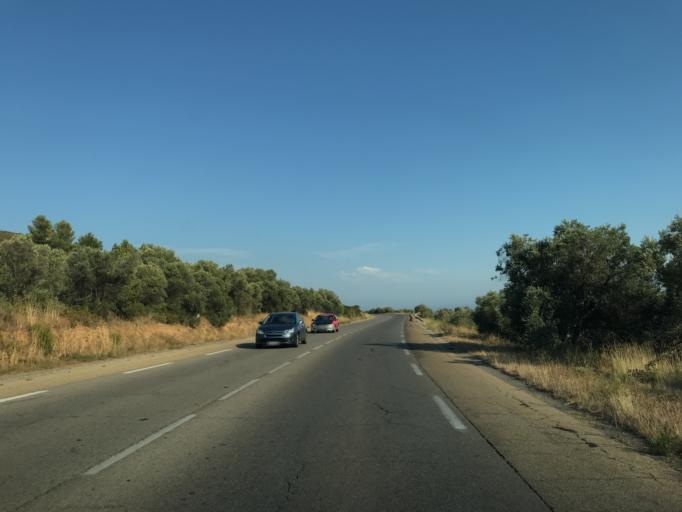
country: FR
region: Provence-Alpes-Cote d'Azur
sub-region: Departement des Bouches-du-Rhone
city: Saint-Chamas
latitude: 43.5311
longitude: 5.0525
